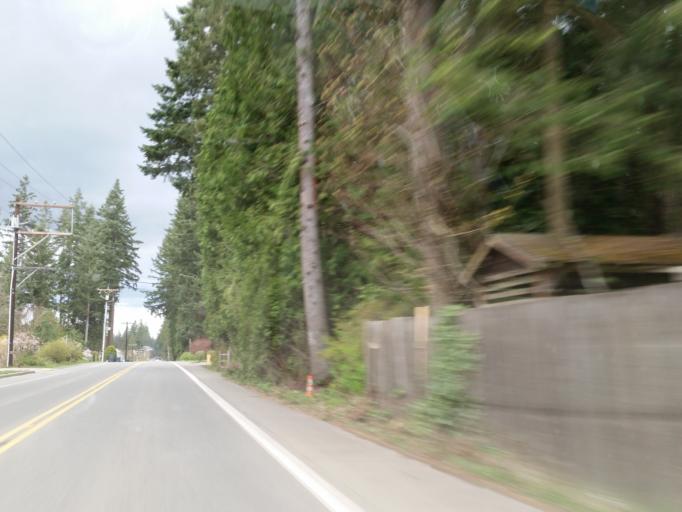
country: US
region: Washington
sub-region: Snohomish County
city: North Creek
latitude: 47.7948
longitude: -122.1730
